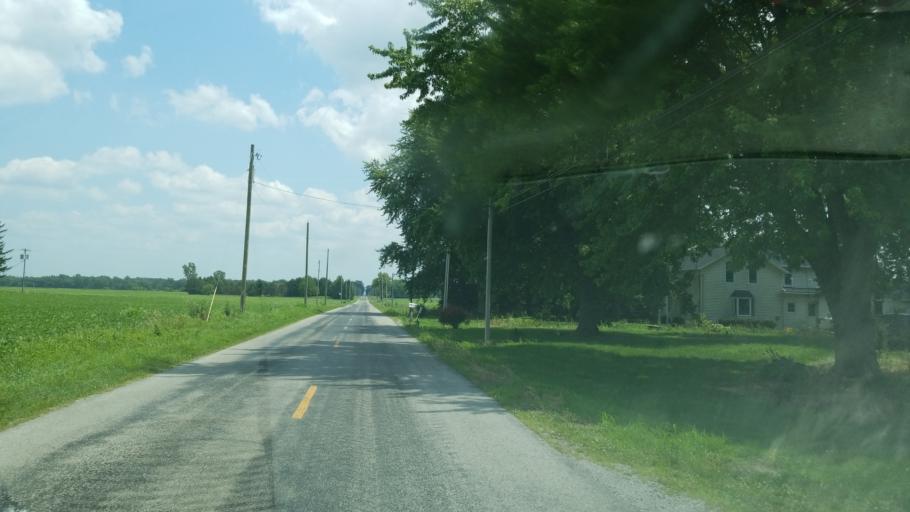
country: US
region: Ohio
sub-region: Henry County
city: Napoleon
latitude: 41.3415
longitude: -84.0984
